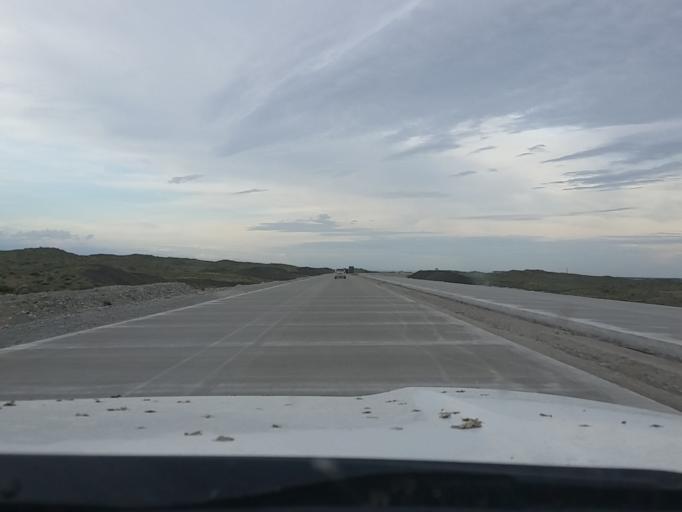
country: KZ
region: Almaty Oblysy
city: Zharkent
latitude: 44.1743
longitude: 80.3266
